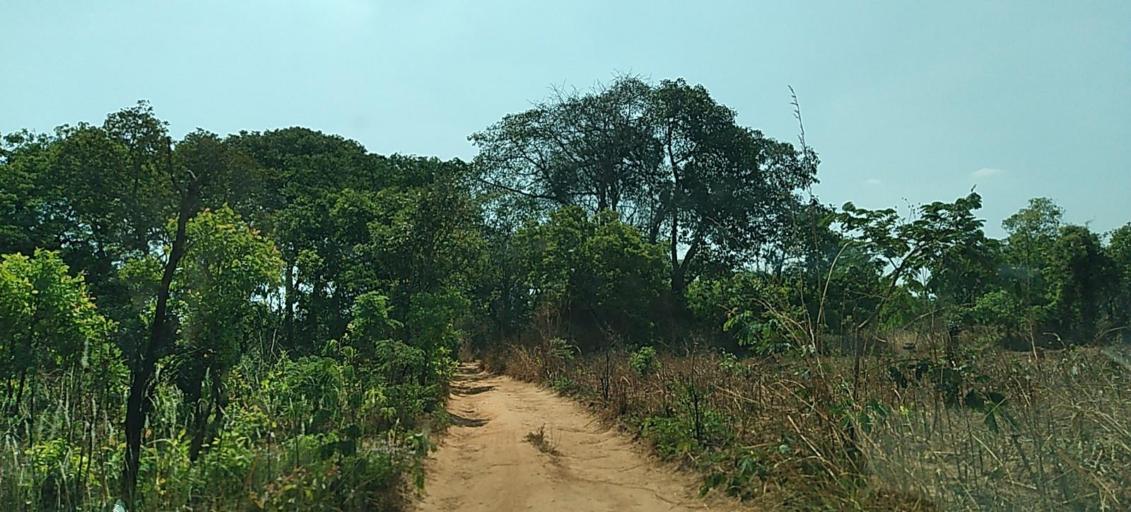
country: ZM
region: North-Western
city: Solwezi
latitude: -12.1009
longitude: 26.2861
